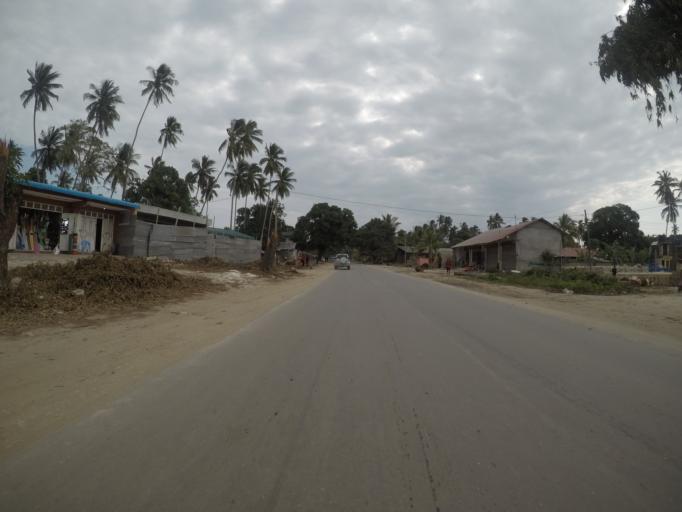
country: TZ
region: Zanzibar Central/South
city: Koani
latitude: -6.1956
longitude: 39.2677
